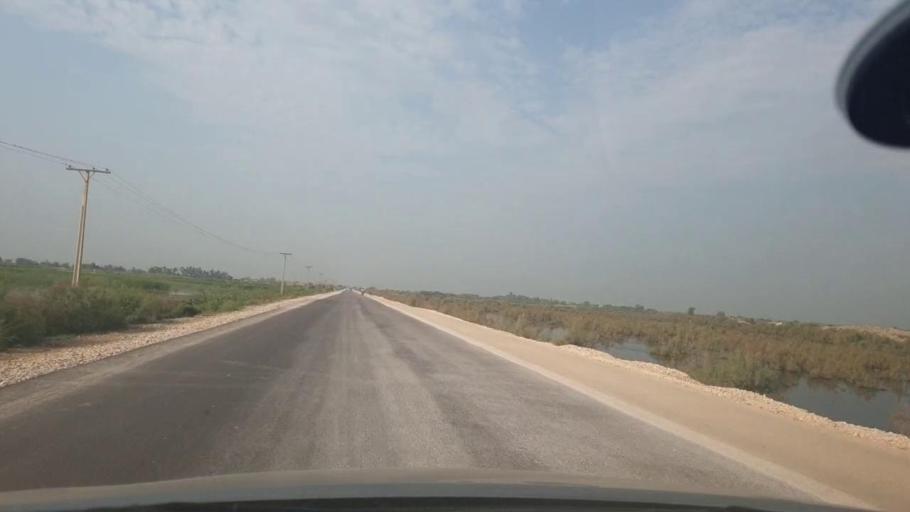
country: PK
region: Sindh
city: Jacobabad
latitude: 28.1462
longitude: 68.3467
